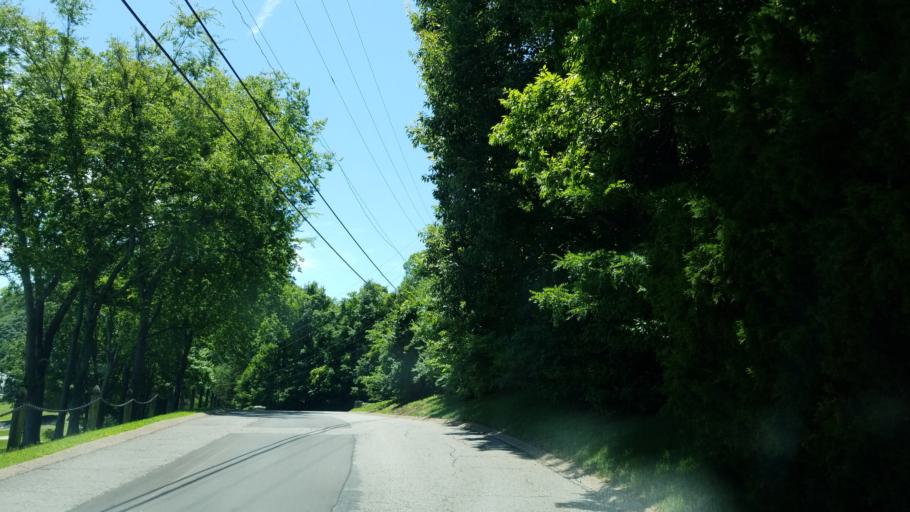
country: US
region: Tennessee
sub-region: Davidson County
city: Forest Hills
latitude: 36.0512
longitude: -86.8195
